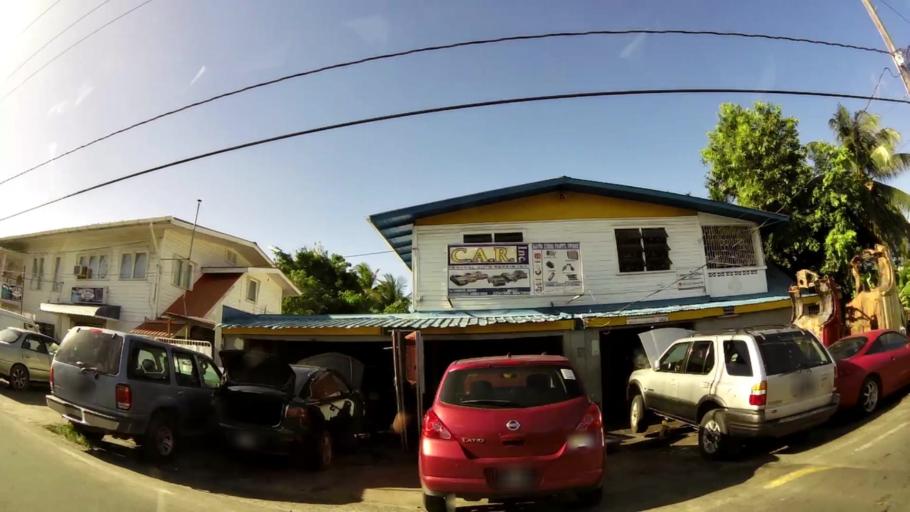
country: GY
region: Demerara-Mahaica
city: Georgetown
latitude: 6.8167
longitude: -58.1388
